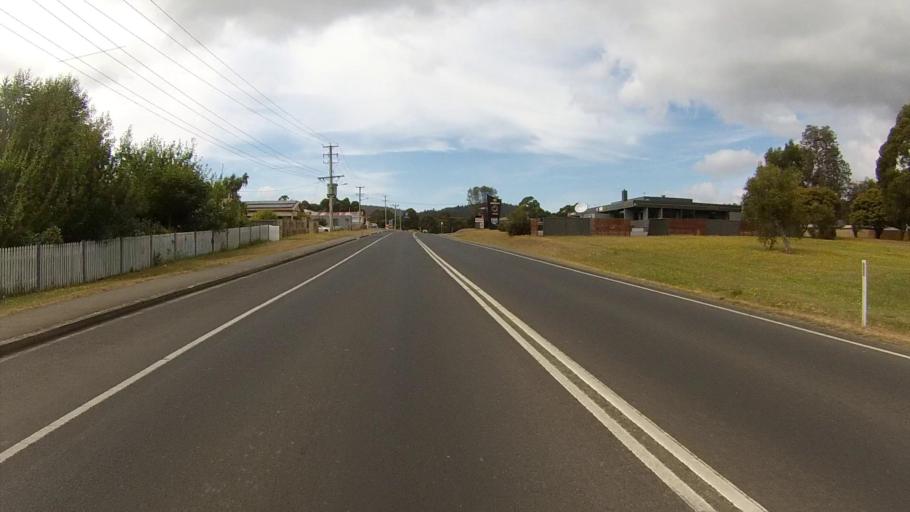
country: AU
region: Tasmania
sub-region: Kingborough
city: Margate
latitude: -43.0674
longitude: 147.2558
